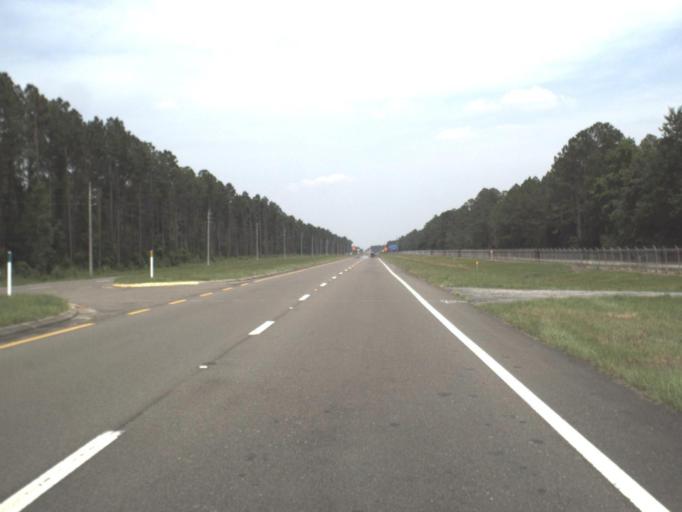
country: US
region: Florida
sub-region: Duval County
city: Baldwin
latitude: 30.2462
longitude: -81.8742
